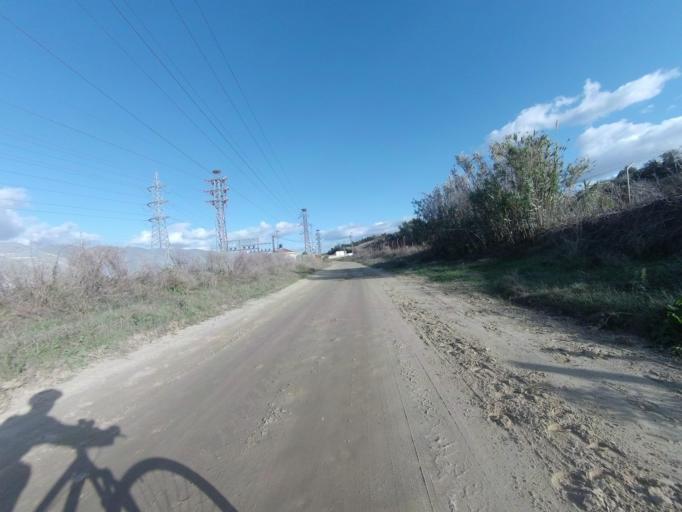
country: ES
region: Andalusia
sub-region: Provincia de Huelva
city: Moguer
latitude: 37.2655
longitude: -6.8526
